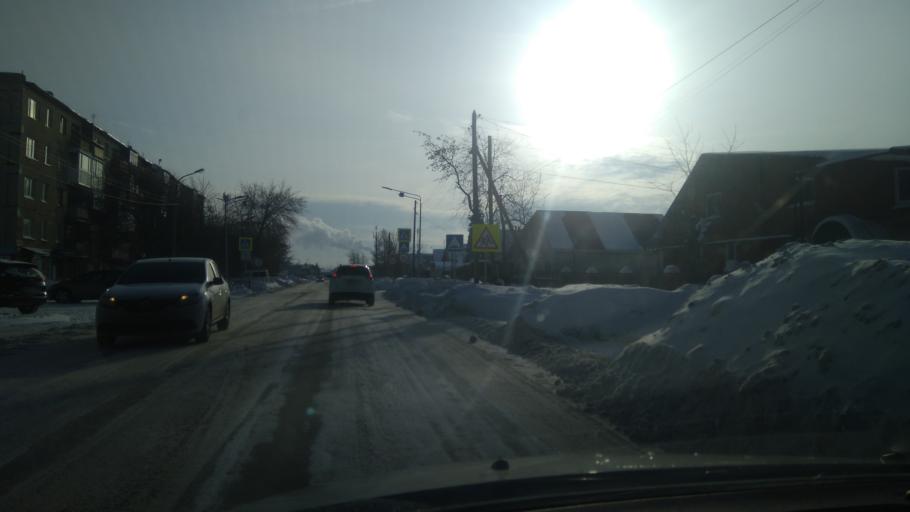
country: RU
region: Sverdlovsk
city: Sukhoy Log
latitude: 56.8948
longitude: 62.0324
